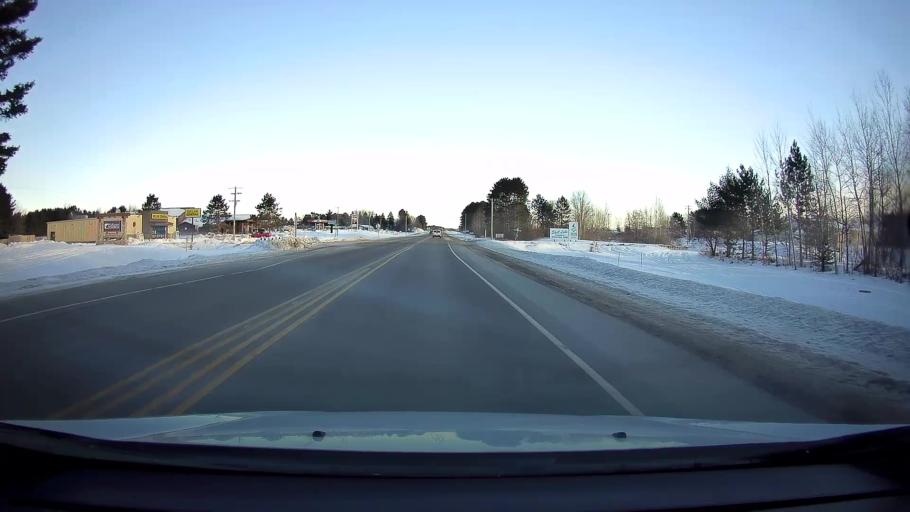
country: US
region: Wisconsin
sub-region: Washburn County
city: Shell Lake
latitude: 45.7313
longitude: -91.9308
